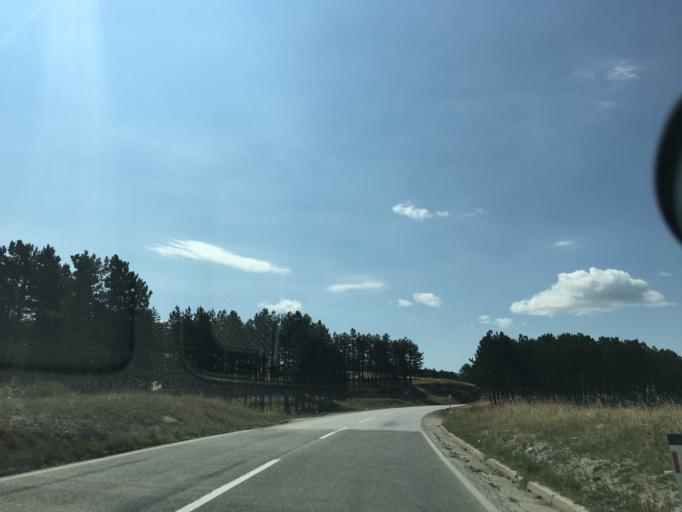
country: RS
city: Zlatibor
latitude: 43.7123
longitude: 19.6896
